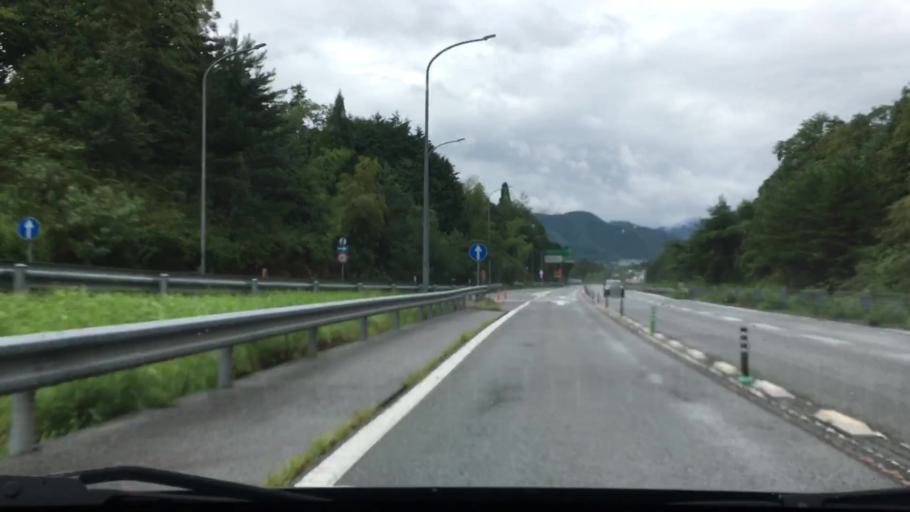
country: JP
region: Hyogo
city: Toyooka
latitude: 35.2936
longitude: 134.8250
